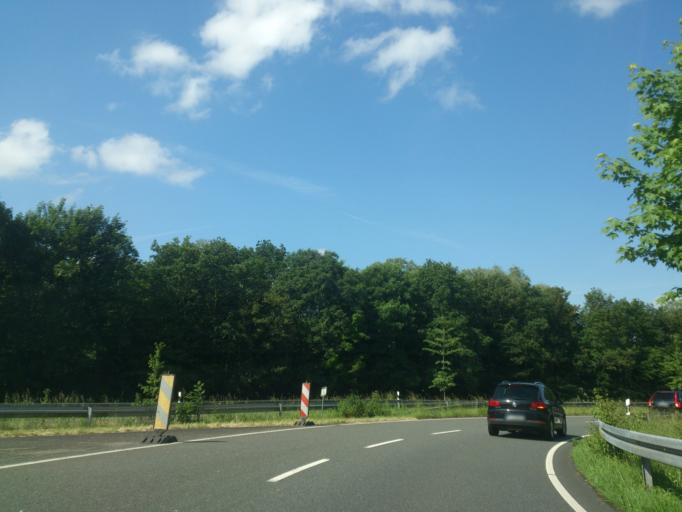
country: DE
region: Lower Saxony
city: Hannover
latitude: 52.3877
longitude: 9.6885
